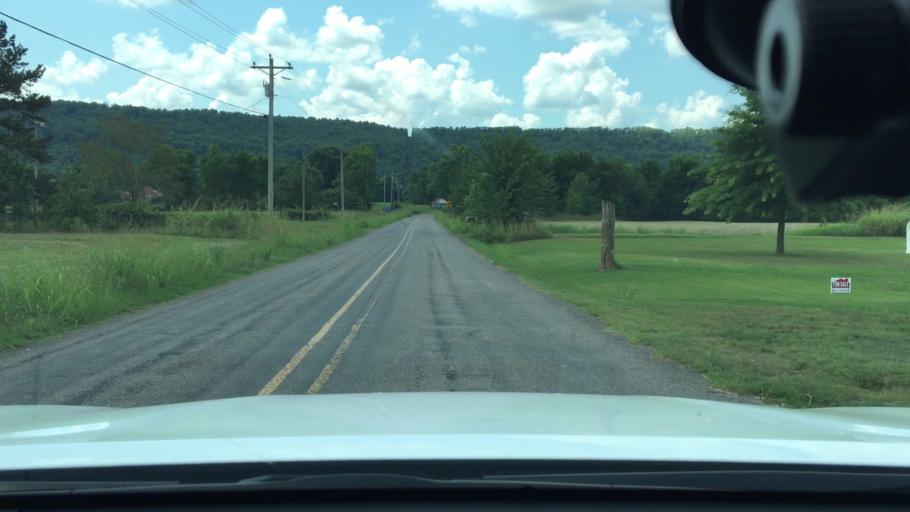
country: US
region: Arkansas
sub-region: Logan County
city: Paris
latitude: 35.2711
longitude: -93.6516
